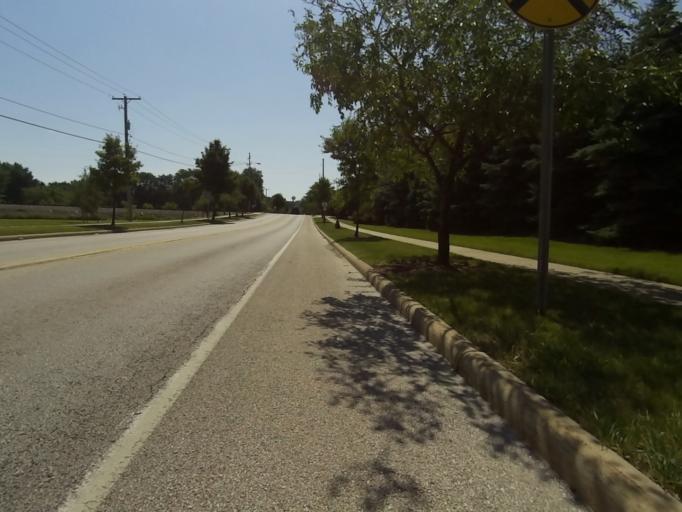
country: US
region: Ohio
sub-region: Portage County
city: Kent
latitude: 41.1637
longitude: -81.3751
